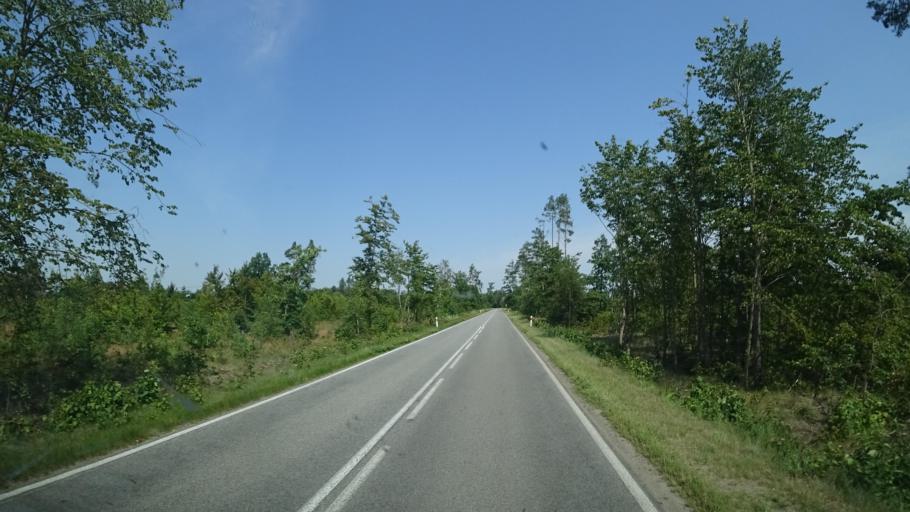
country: PL
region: Pomeranian Voivodeship
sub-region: Powiat chojnicki
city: Brusy
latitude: 53.9412
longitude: 17.7451
